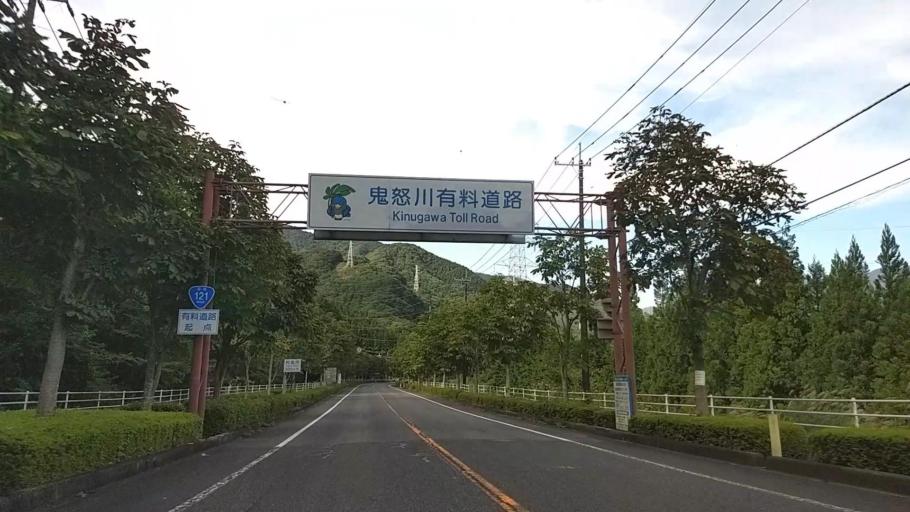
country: JP
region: Tochigi
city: Imaichi
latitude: 36.8131
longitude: 139.7070
